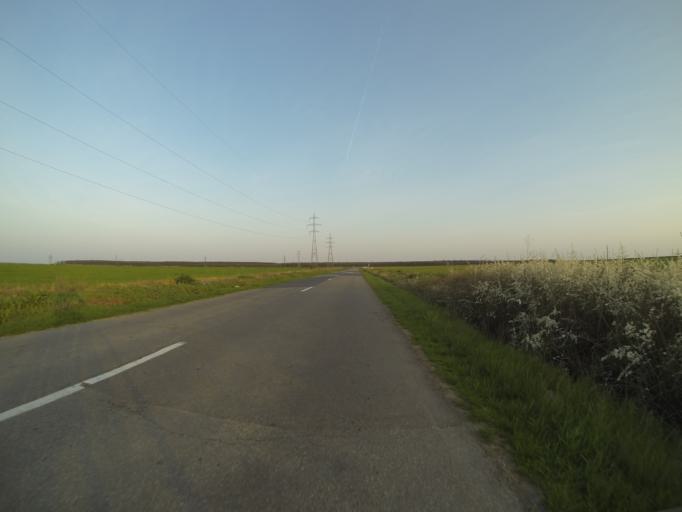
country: RO
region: Dolj
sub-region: Comuna Segarcea
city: Segarcea
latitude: 44.0726
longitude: 23.7954
